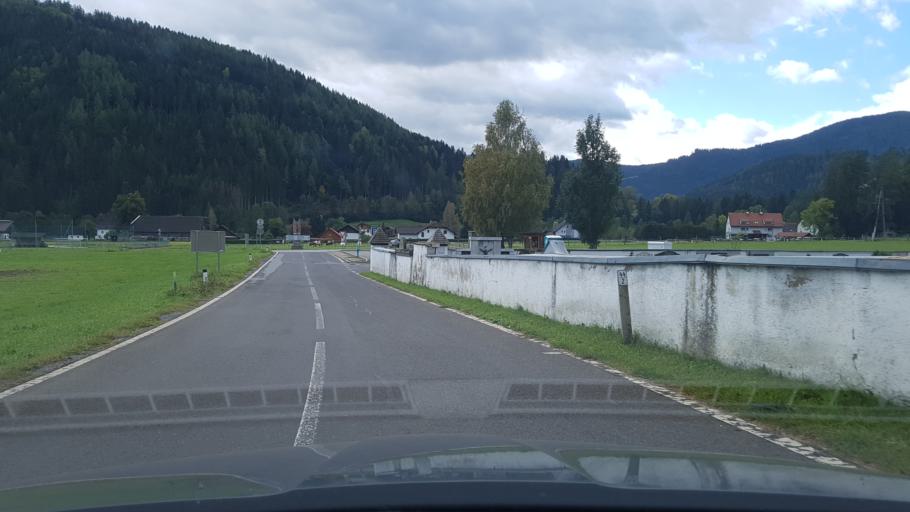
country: AT
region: Styria
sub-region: Politischer Bezirk Murau
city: Schoder
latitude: 47.1846
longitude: 14.1182
